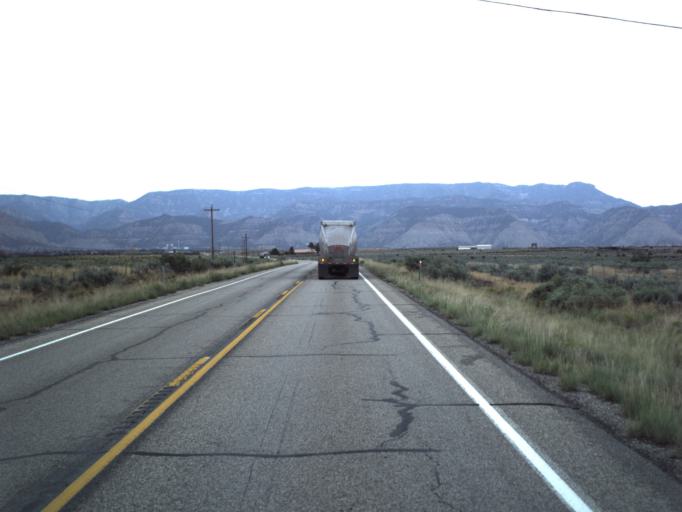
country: US
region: Utah
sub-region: Carbon County
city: East Carbon City
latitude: 39.5355
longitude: -110.4705
